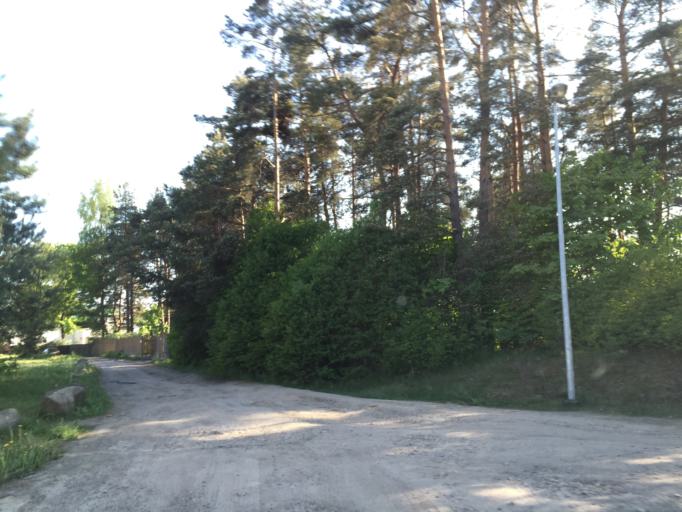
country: LV
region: Kekava
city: Balozi
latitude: 56.8977
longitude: 24.1376
